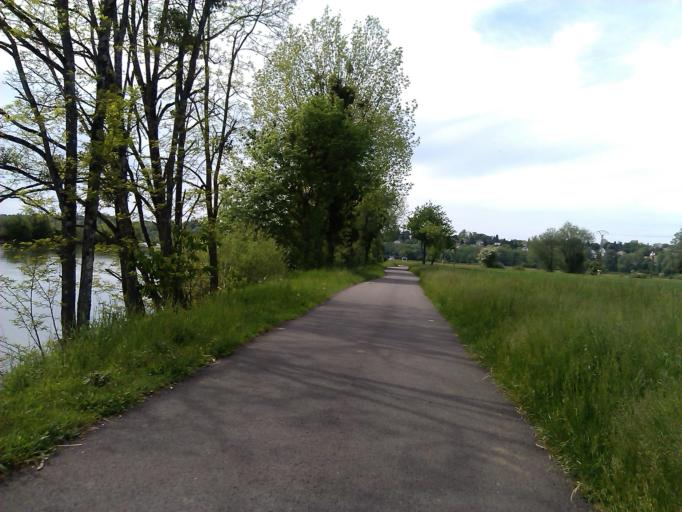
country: FR
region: Franche-Comte
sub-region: Departement du Doubs
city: Saint-Vit
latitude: 47.1713
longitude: 5.8089
